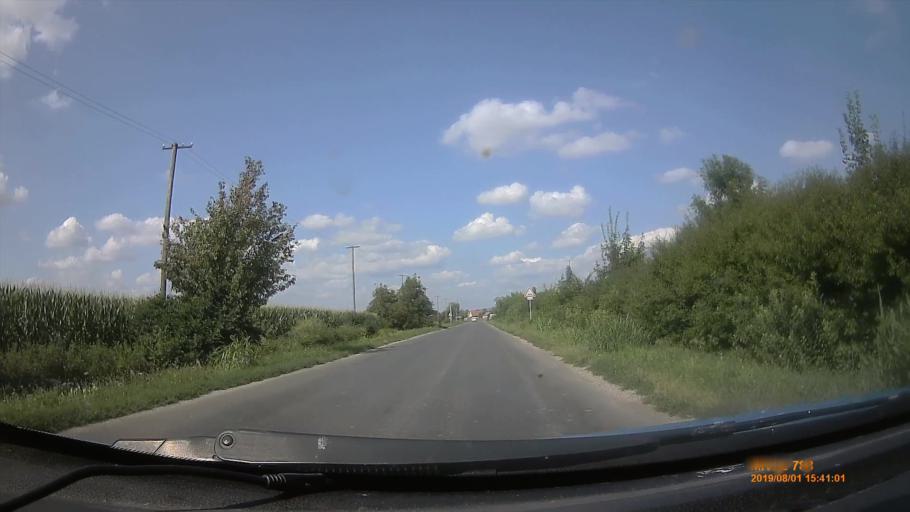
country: HU
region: Baranya
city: Szentlorinc
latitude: 45.9874
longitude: 17.9588
